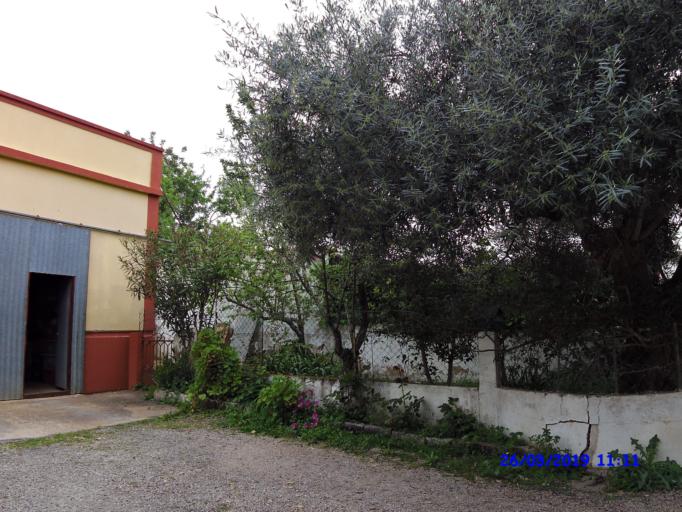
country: PT
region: Faro
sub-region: Loule
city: Boliqueime
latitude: 37.1651
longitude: -8.1974
